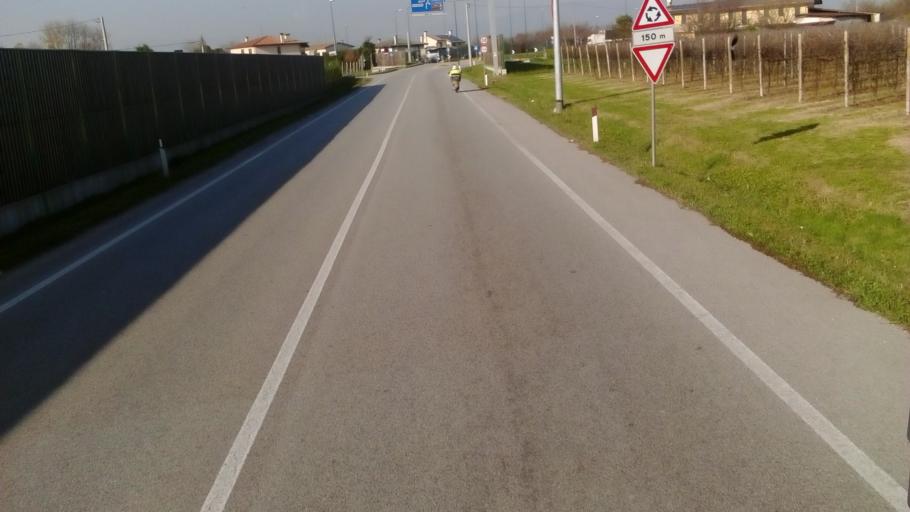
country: IT
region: Veneto
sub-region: Provincia di Treviso
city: Varago
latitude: 45.7368
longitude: 12.2795
